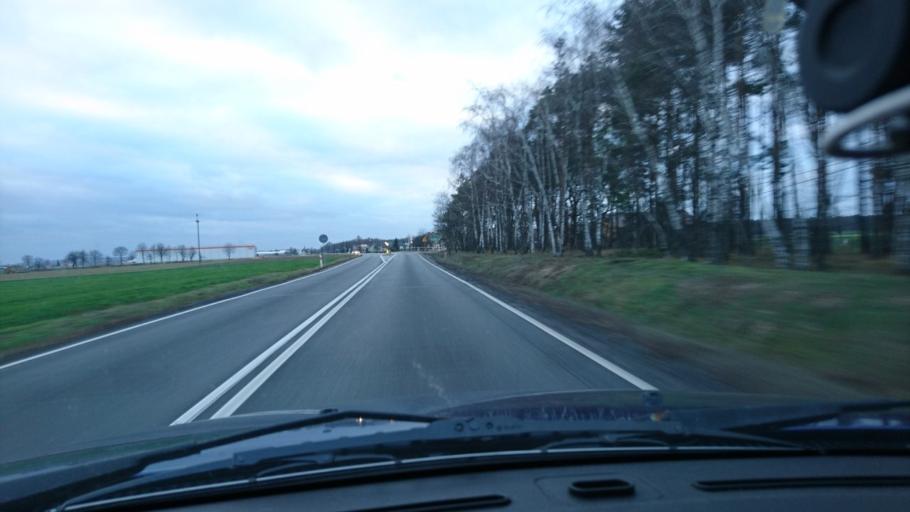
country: PL
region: Greater Poland Voivodeship
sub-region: Powiat kepinski
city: Leka Opatowska
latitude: 51.2241
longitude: 18.1112
